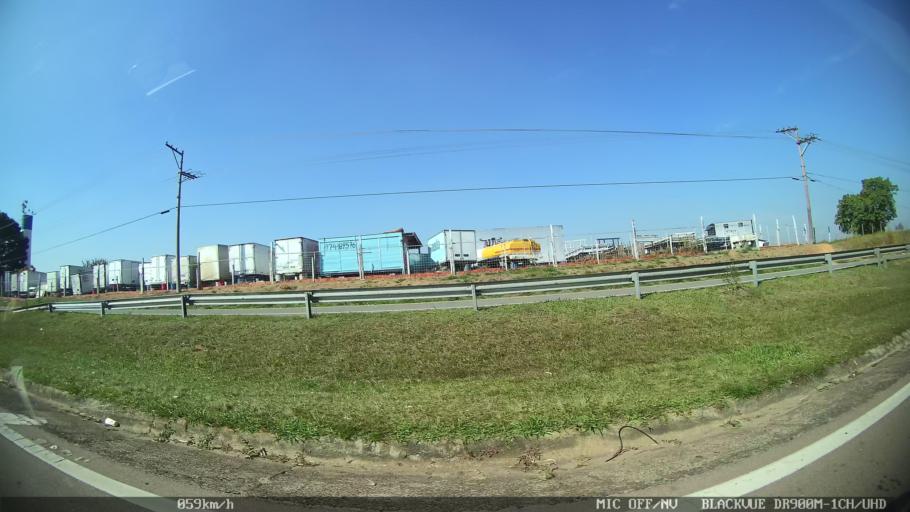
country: BR
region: Sao Paulo
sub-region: Campinas
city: Campinas
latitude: -22.9887
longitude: -47.1070
